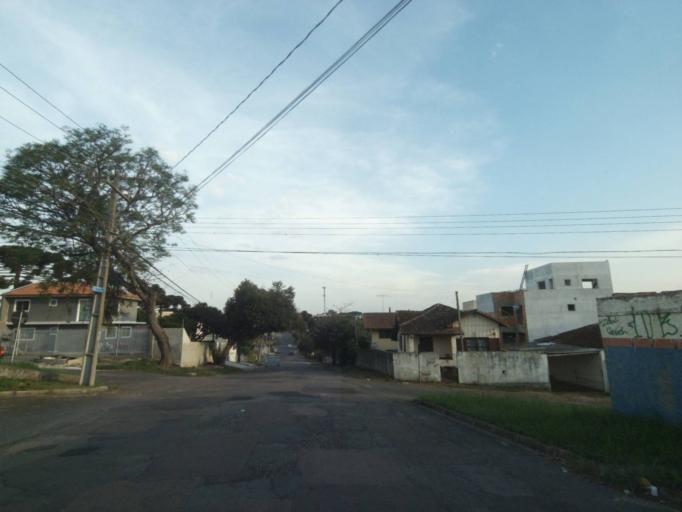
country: BR
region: Parana
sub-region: Curitiba
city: Curitiba
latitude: -25.4650
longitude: -49.3071
